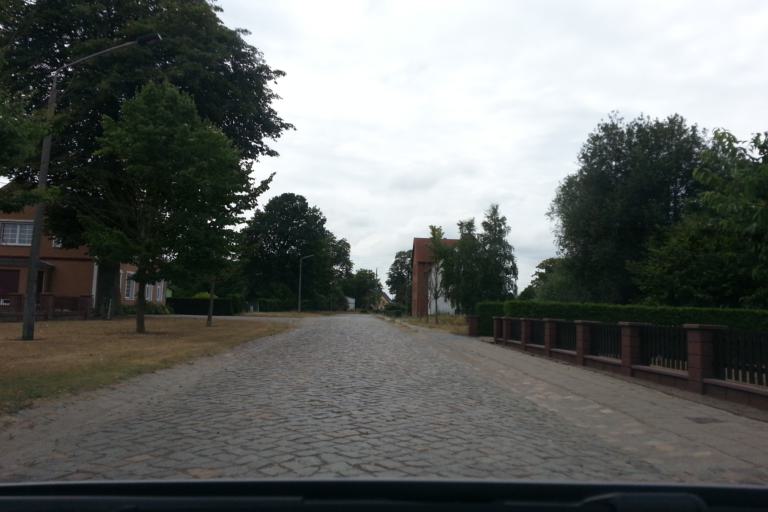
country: DE
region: Mecklenburg-Vorpommern
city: Ferdinandshof
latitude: 53.6582
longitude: 13.8861
